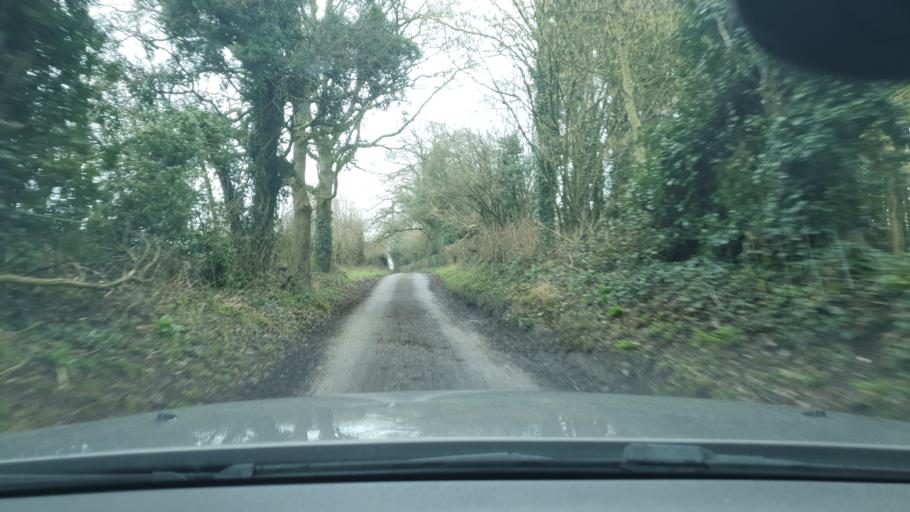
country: GB
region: England
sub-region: Wiltshire
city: Ramsbury
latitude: 51.4658
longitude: -1.5919
